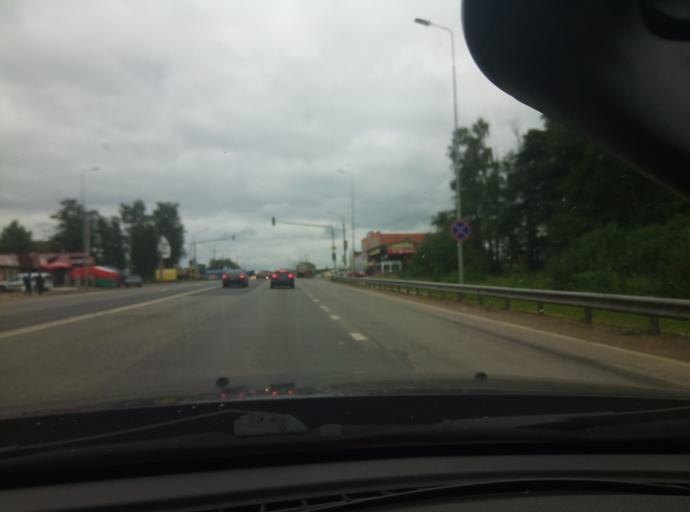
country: RU
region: Kaluga
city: Belousovo
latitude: 55.1069
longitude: 36.6422
